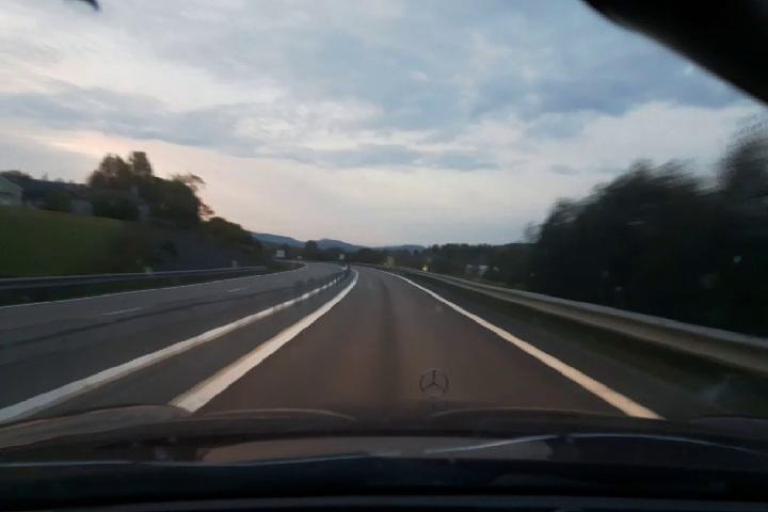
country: SE
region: Vaesternorrland
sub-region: Kramfors Kommun
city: Nordingra
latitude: 62.9746
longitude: 18.1606
